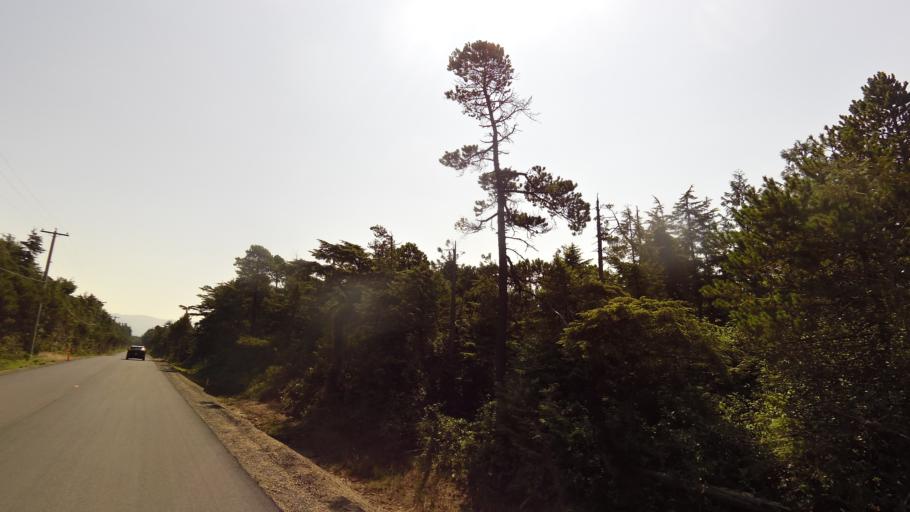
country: CA
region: British Columbia
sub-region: Regional District of Alberni-Clayoquot
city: Ucluelet
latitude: 49.0154
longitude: -125.6665
